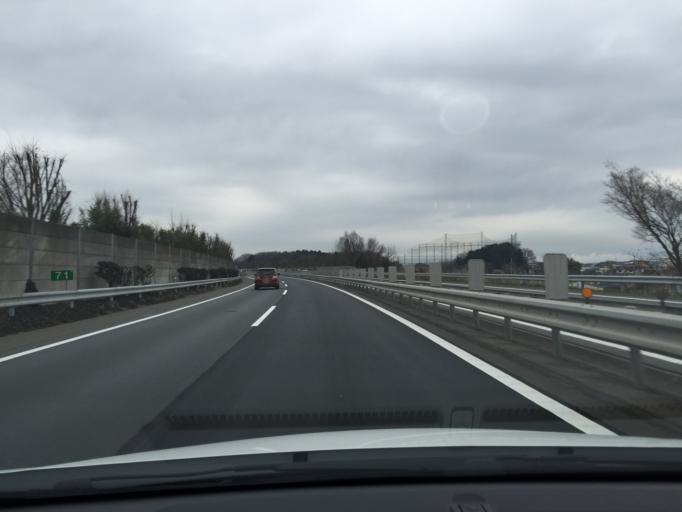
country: JP
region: Saitama
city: Sayama
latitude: 35.8802
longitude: 139.3800
